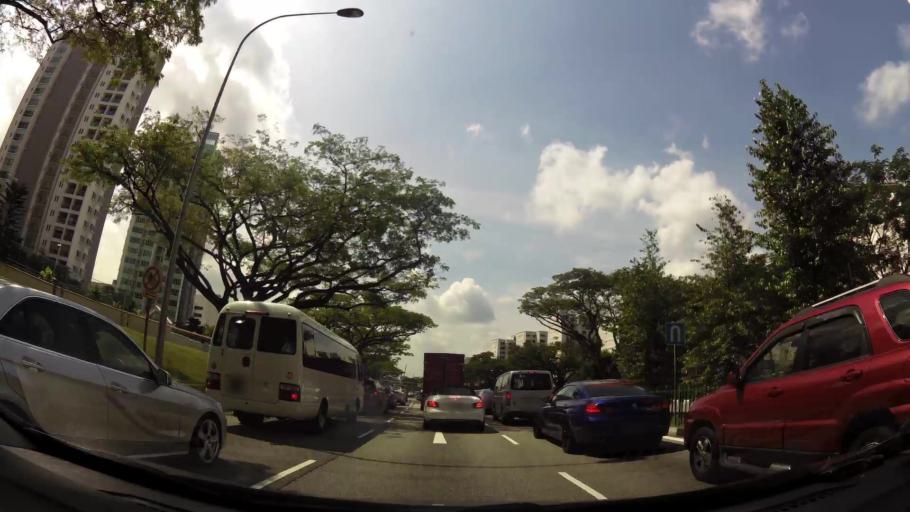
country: SG
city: Singapore
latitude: 1.3521
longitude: 103.8402
